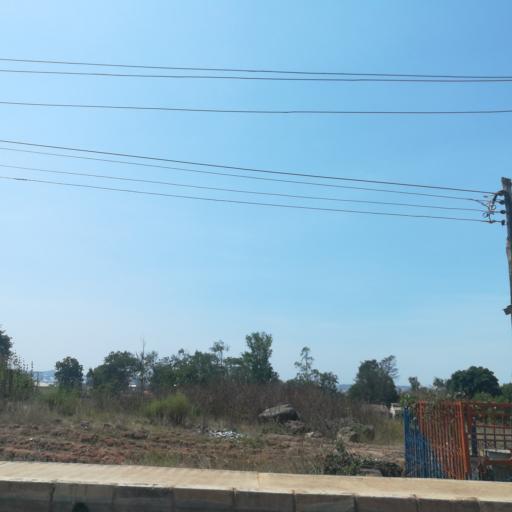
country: NG
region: Plateau
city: Bukuru
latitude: 9.8448
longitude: 8.9007
